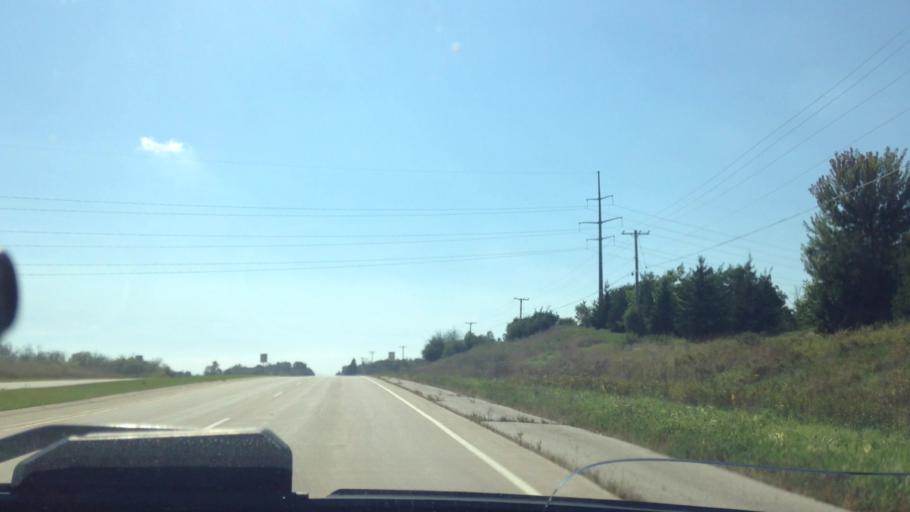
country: US
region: Wisconsin
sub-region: Ozaukee County
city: Port Washington
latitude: 43.3656
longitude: -87.9036
